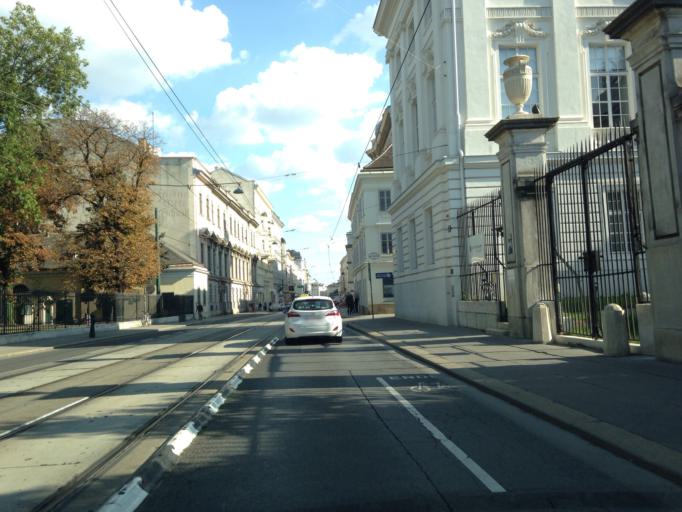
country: AT
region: Vienna
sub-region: Wien Stadt
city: Vienna
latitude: 48.2195
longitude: 16.3571
